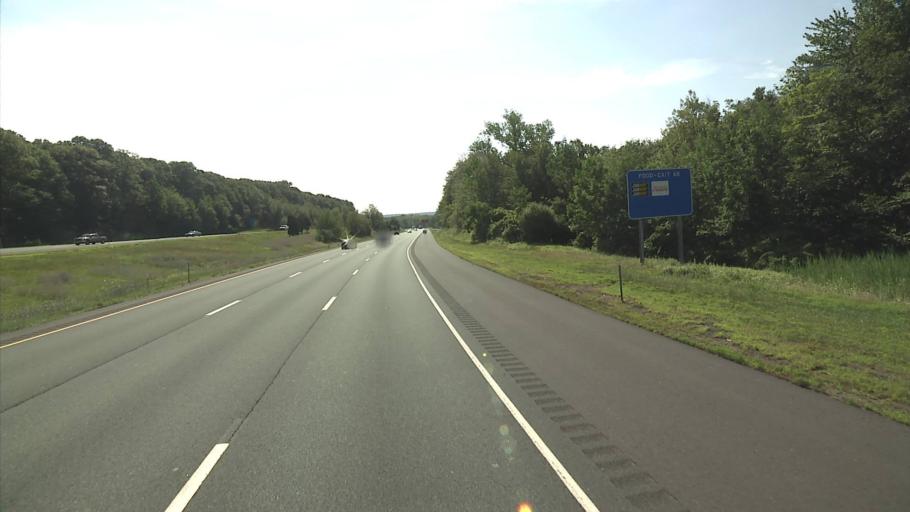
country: US
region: Connecticut
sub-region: Tolland County
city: Tolland
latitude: 41.8554
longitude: -72.3977
